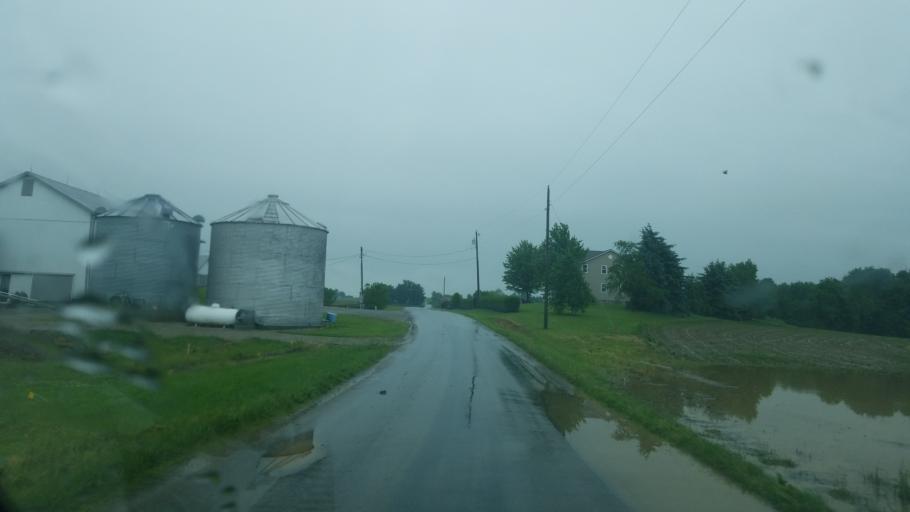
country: US
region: Ohio
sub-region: Huron County
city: Plymouth
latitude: 40.9862
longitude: -82.5967
